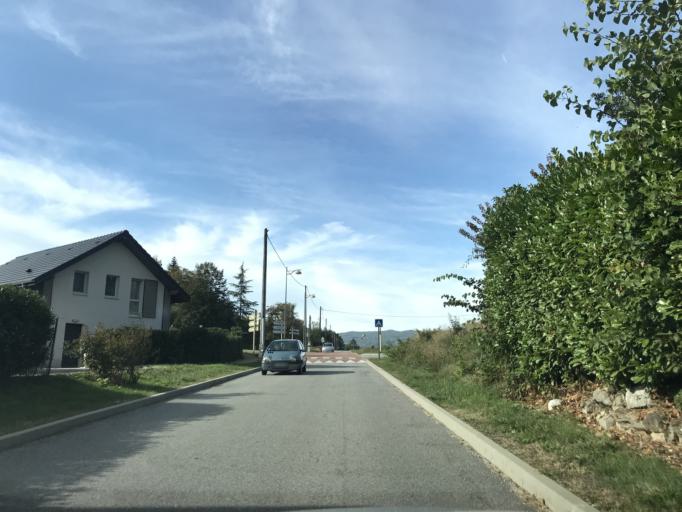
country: FR
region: Rhone-Alpes
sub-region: Departement de la Savoie
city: Yenne
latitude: 45.6764
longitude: 5.7838
